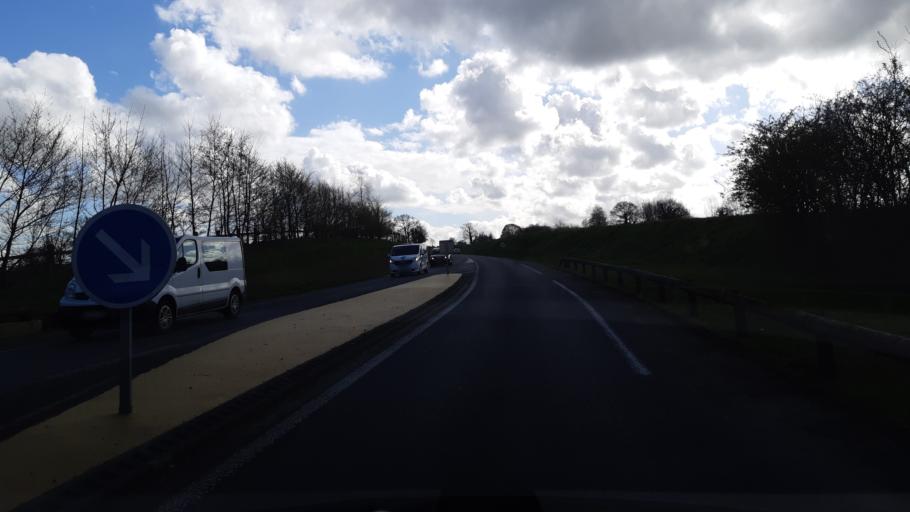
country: FR
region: Lower Normandy
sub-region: Departement de la Manche
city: Agneaux
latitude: 49.0690
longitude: -1.1300
